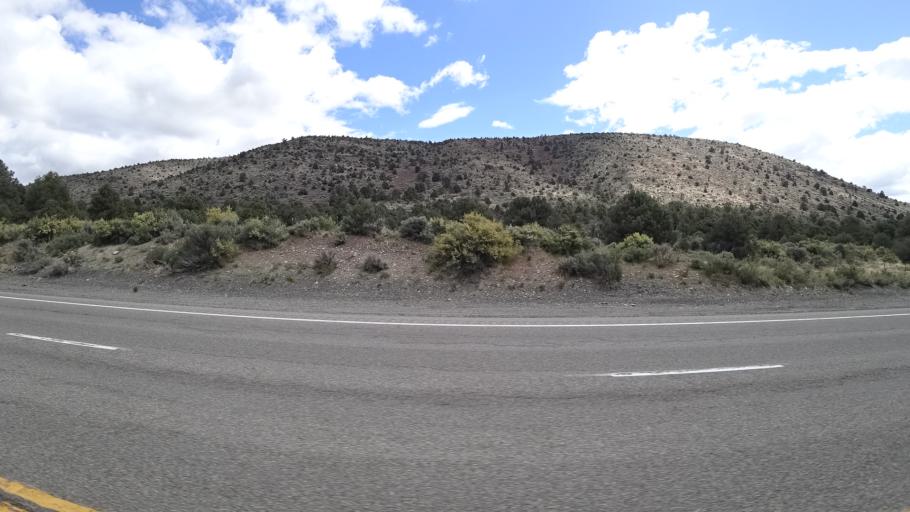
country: US
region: Nevada
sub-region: Douglas County
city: Gardnerville Ranchos
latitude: 38.7623
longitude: -119.5768
